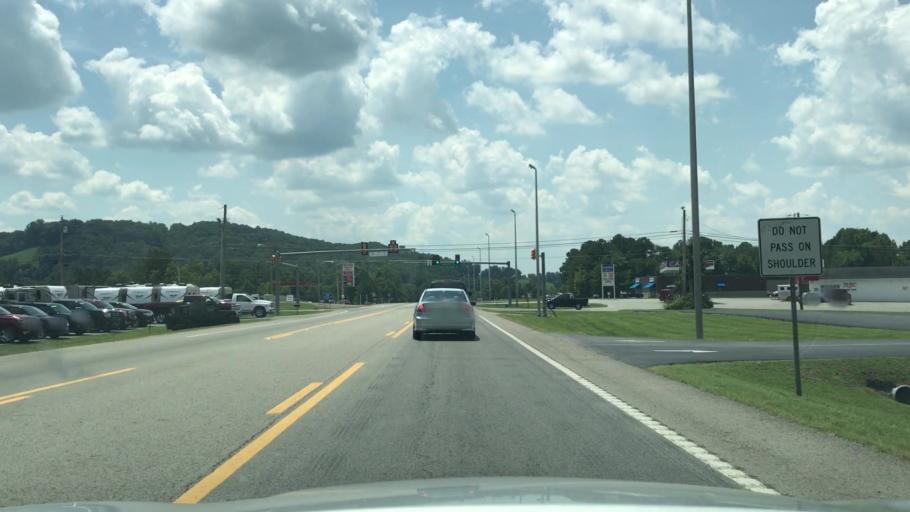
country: US
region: Tennessee
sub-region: Overton County
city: Livingston
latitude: 36.3873
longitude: -85.3348
